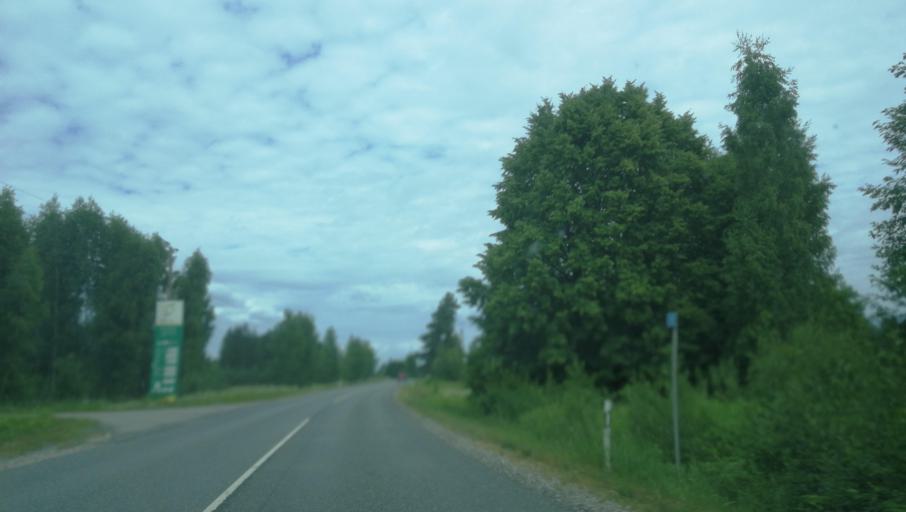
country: LV
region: Naukseni
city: Naukseni
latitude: 57.7264
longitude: 25.4219
